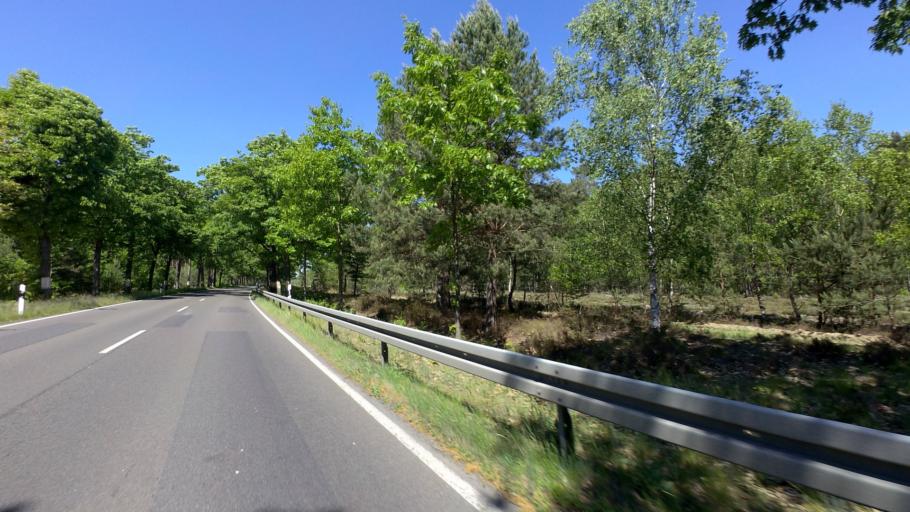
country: DE
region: Brandenburg
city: Drehnow
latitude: 51.9017
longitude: 14.3562
